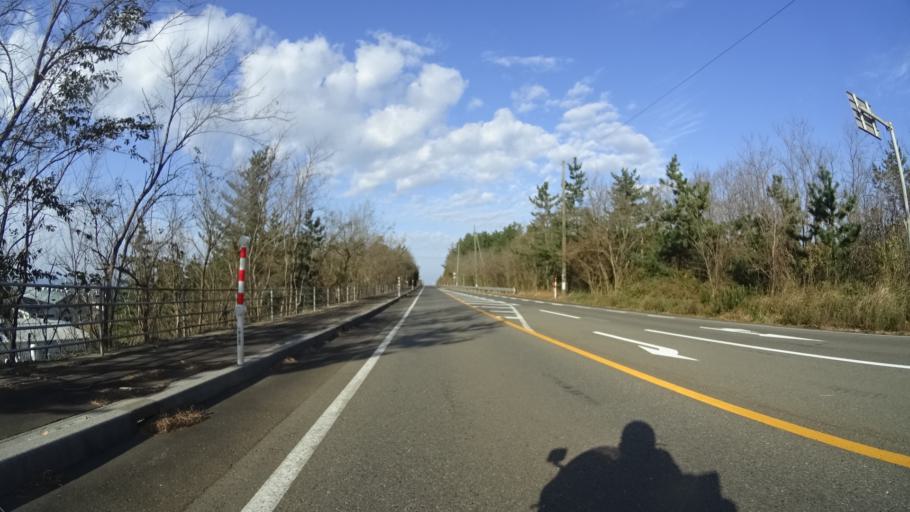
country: JP
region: Niigata
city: Kashiwazaki
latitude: 37.2844
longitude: 138.3990
